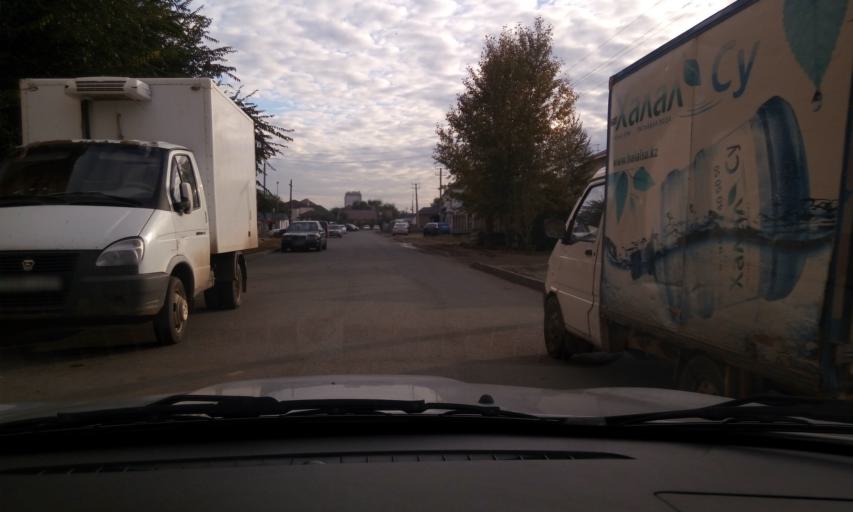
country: KZ
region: Astana Qalasy
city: Astana
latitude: 51.1406
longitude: 71.4862
